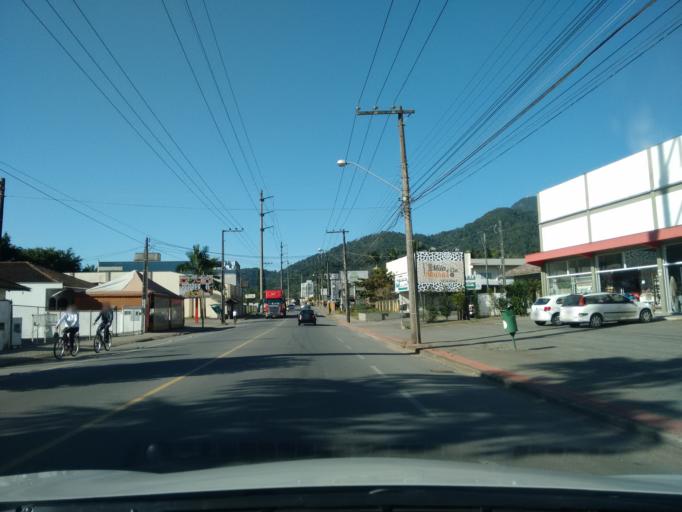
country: BR
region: Santa Catarina
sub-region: Jaragua Do Sul
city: Jaragua do Sul
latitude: -26.5070
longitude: -49.0969
